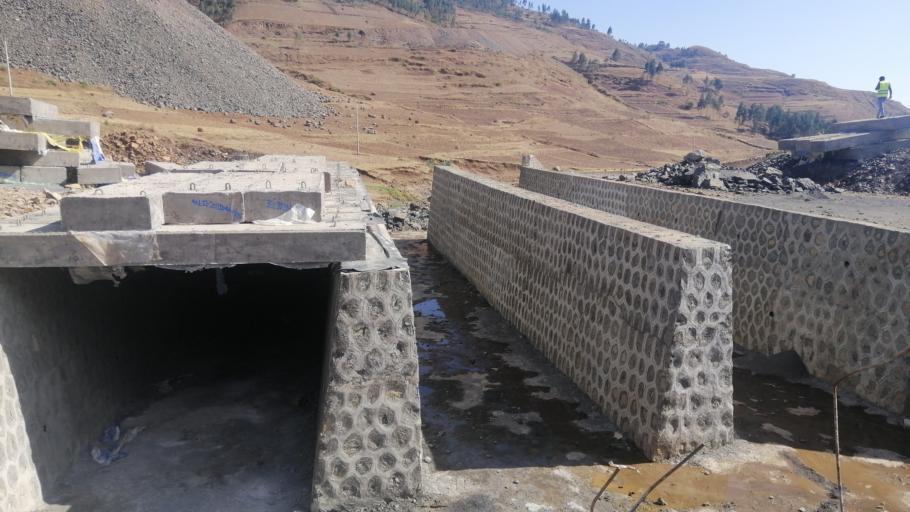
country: ET
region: Amhara
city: Debre Tabor
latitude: 11.4213
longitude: 38.2089
